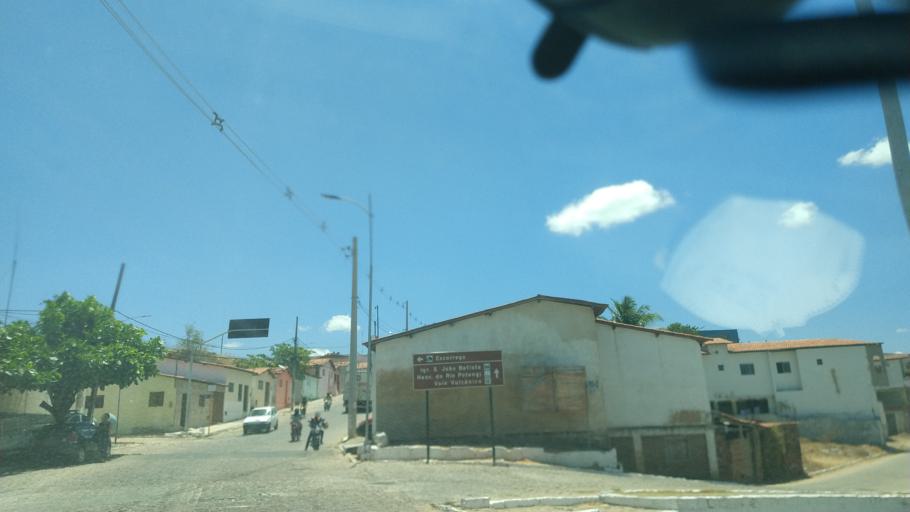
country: BR
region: Rio Grande do Norte
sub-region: Cerro Cora
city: Cerro Cora
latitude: -6.0424
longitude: -36.3463
